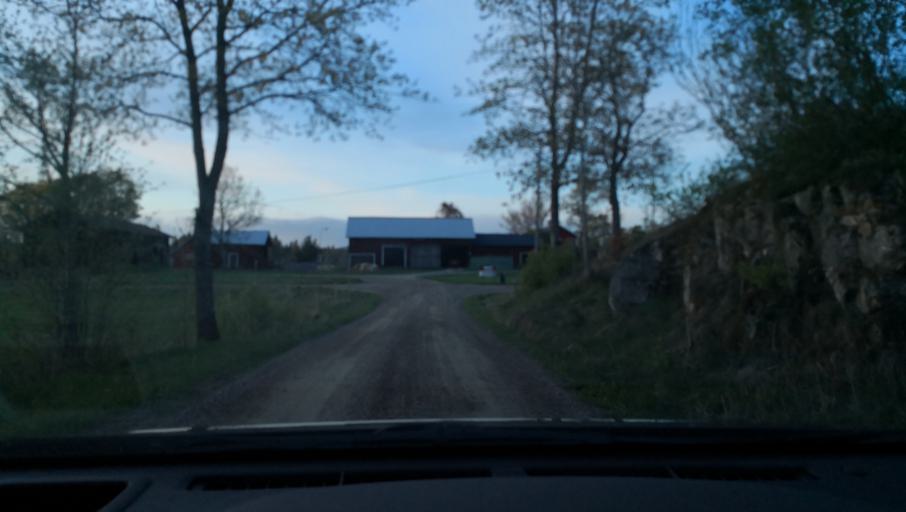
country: SE
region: OErebro
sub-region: Askersunds Kommun
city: Asbro
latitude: 58.9796
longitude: 14.9495
